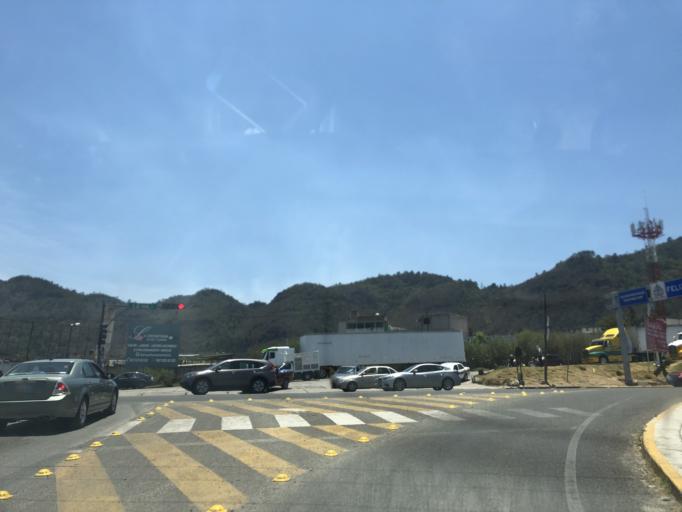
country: MX
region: Chiapas
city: San Cristobal de las Casas
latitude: 16.7222
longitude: -92.6519
